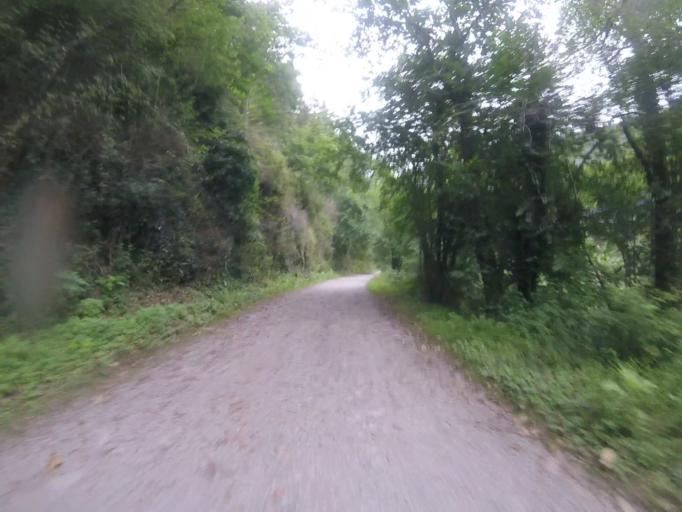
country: ES
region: Navarre
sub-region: Provincia de Navarra
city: Igantzi
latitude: 43.2124
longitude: -1.6724
